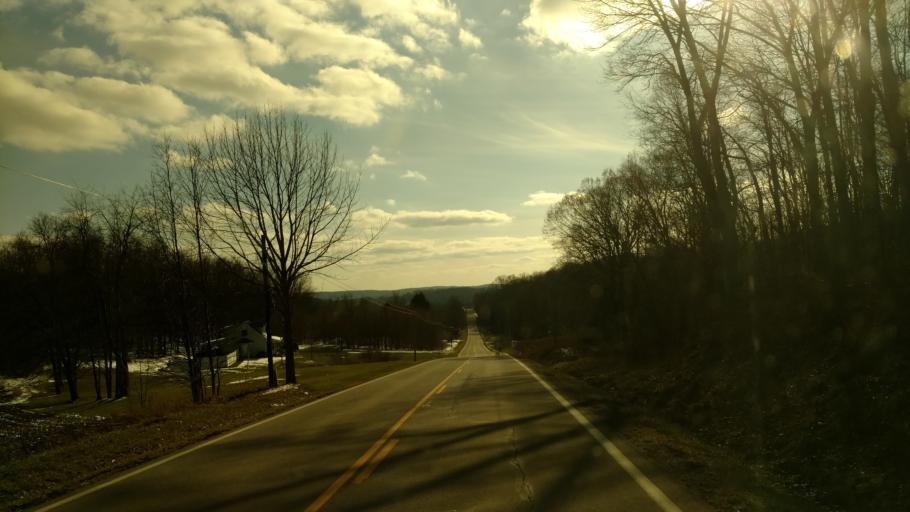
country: US
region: Ohio
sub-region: Ashland County
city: Loudonville
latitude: 40.6922
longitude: -82.2647
